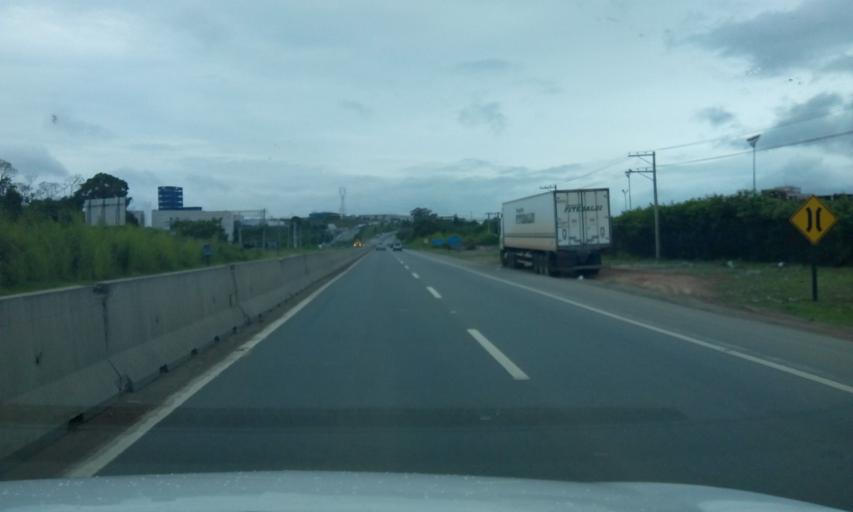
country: BR
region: Sao Paulo
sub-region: Itupeva
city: Itupeva
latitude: -23.1617
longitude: -47.0223
